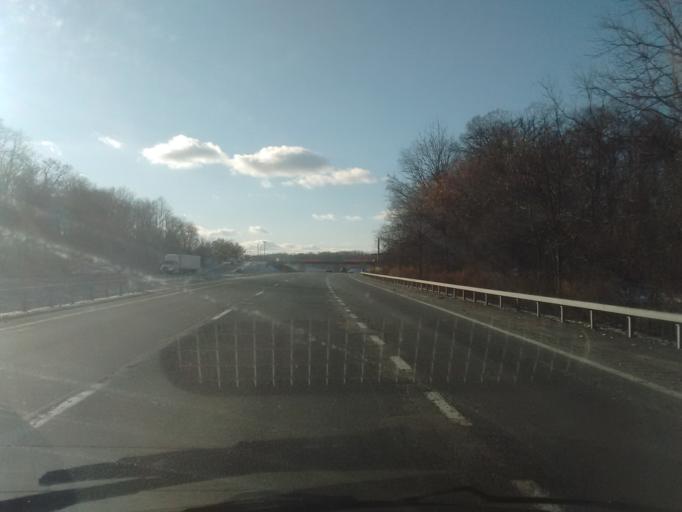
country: US
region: New York
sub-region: Orange County
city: Gardnertown
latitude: 41.5143
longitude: -74.0459
